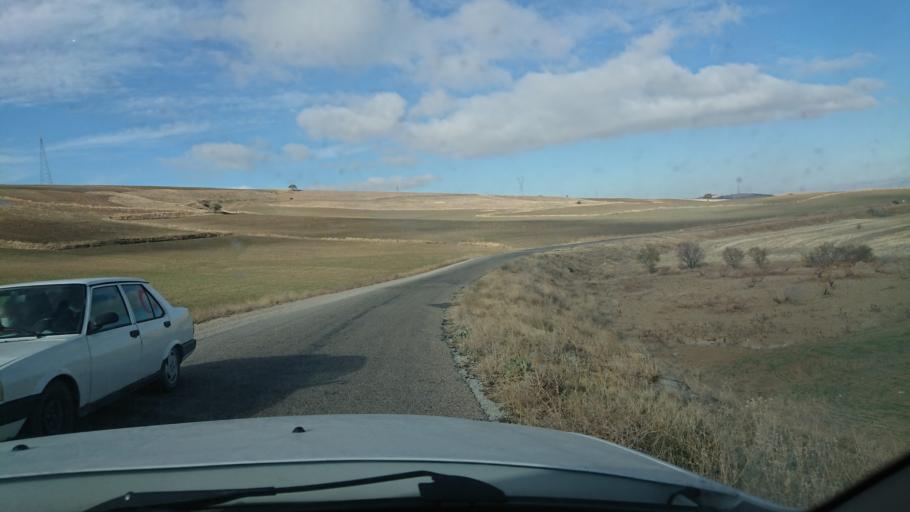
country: TR
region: Aksaray
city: Agacoren
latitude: 38.8440
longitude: 33.9506
